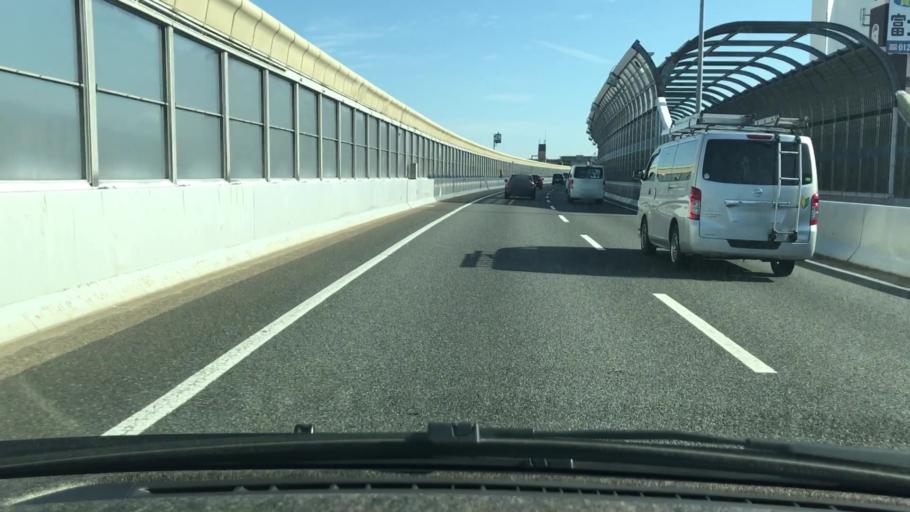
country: JP
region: Hyogo
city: Kobe
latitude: 34.7101
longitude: 135.2426
